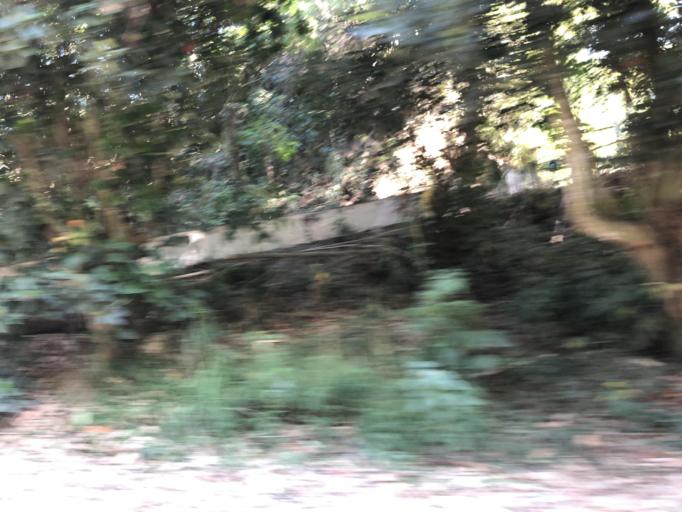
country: TW
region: Taiwan
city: Yujing
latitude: 23.0558
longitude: 120.3790
